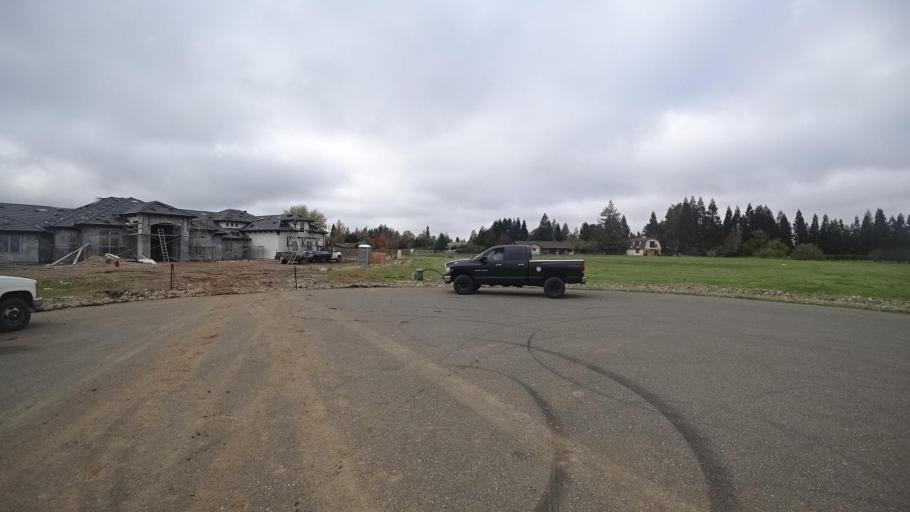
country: US
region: California
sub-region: Sacramento County
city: Wilton
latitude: 38.4471
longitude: -121.3002
